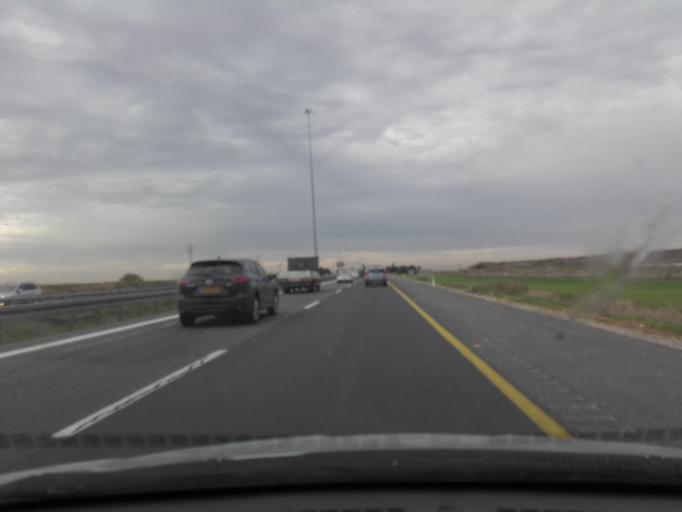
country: IL
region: Central District
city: Ramla
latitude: 31.8949
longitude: 34.8825
